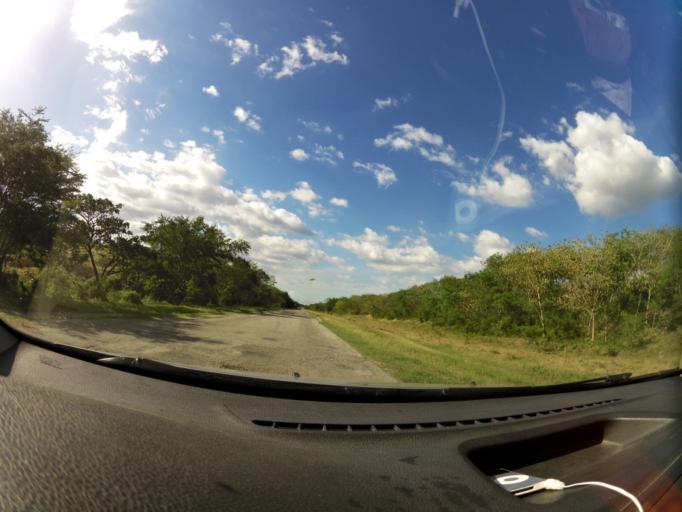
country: CU
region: Santiago de Cuba
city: Palma Soriano
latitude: 20.2460
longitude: -75.9763
